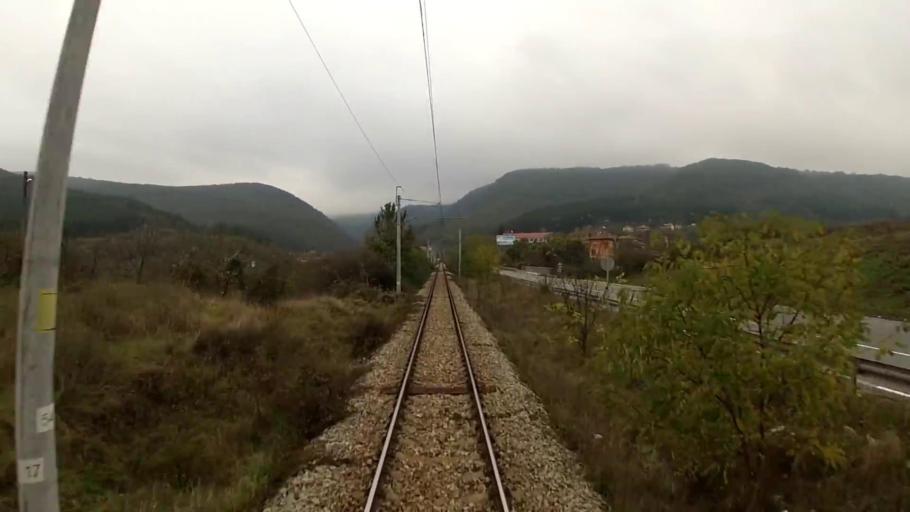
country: RS
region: Central Serbia
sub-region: Pirotski Okrug
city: Dimitrovgrad
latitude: 42.9811
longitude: 22.8502
